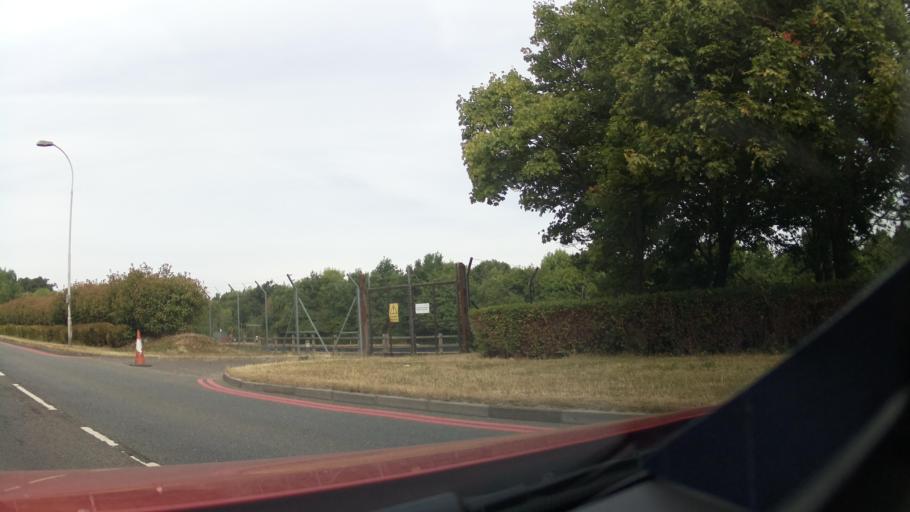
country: GB
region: England
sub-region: Surrey
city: Horley
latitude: 51.1643
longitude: -0.1826
